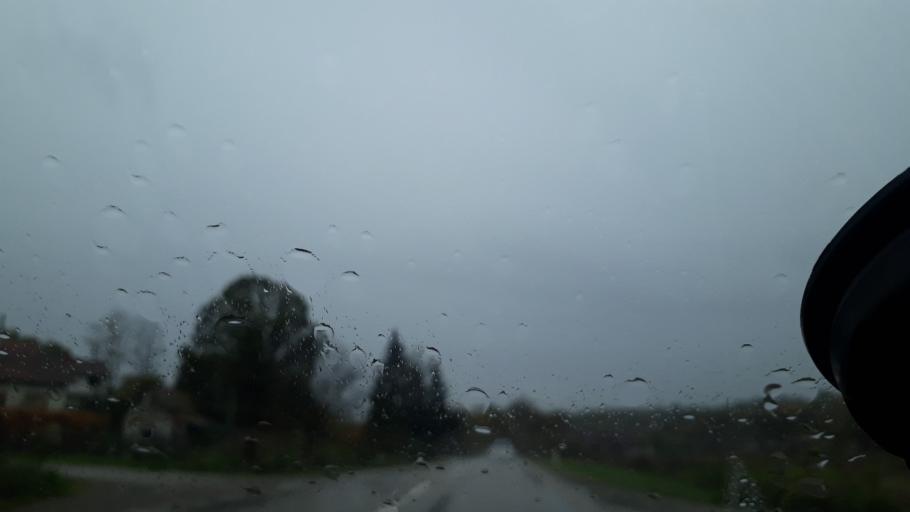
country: BA
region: Republika Srpska
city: Maglajani
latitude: 44.8632
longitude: 17.4343
